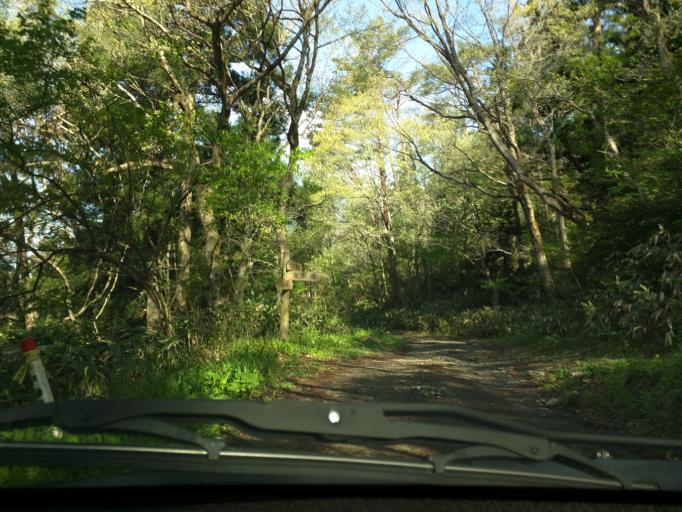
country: JP
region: Fukushima
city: Inawashiro
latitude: 37.5052
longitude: 139.9611
